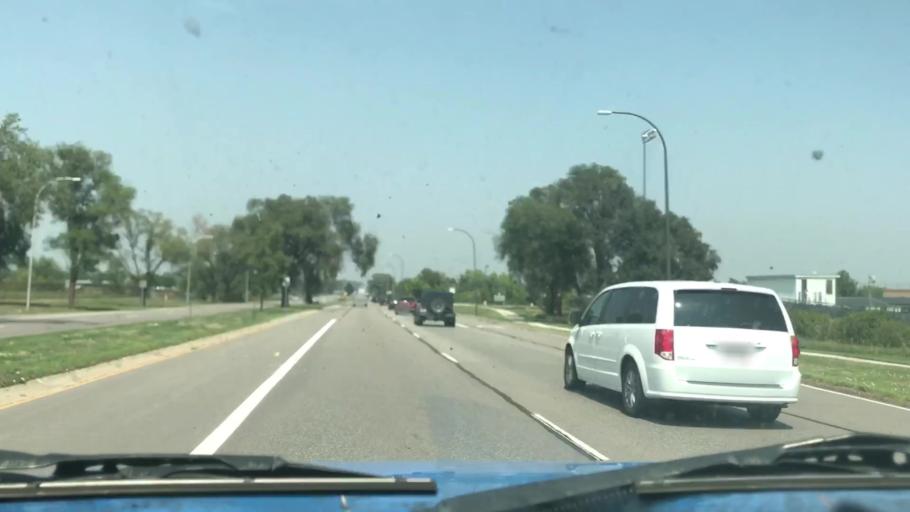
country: US
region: Colorado
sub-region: Jefferson County
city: Lakewood
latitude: 39.7150
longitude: -105.1097
